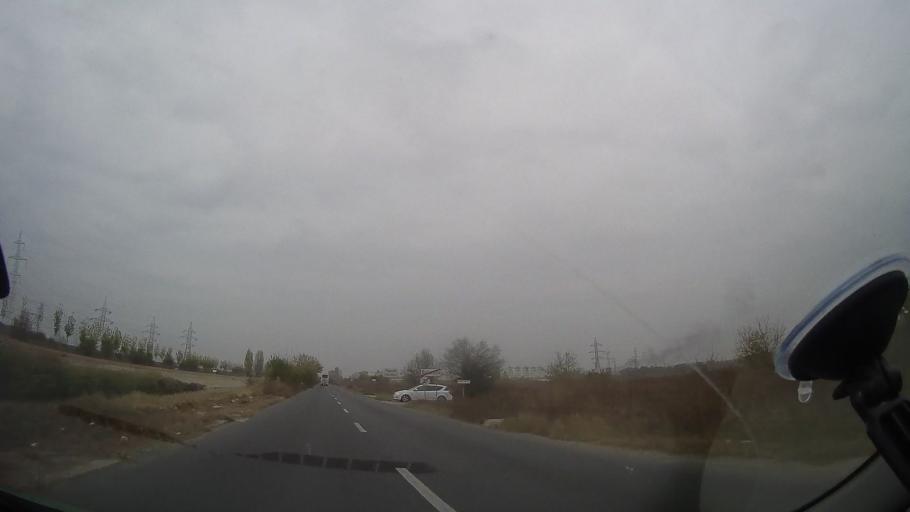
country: RO
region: Ilfov
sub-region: Comuna Glina
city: Catelu
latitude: 44.3951
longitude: 26.2118
